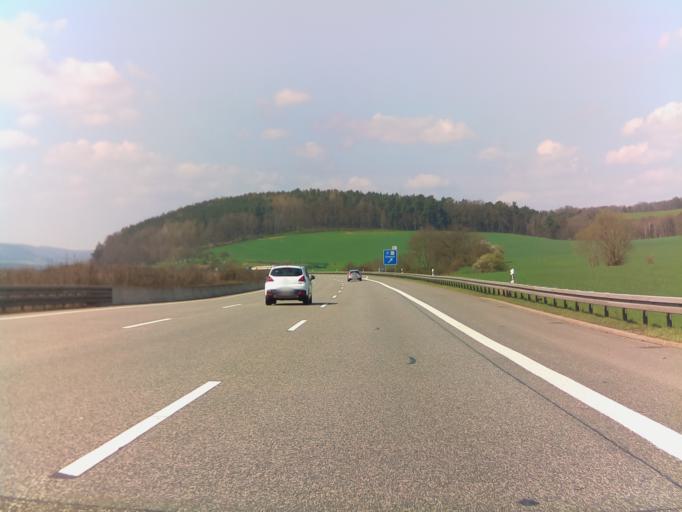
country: DE
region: Thuringia
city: Rausdorf
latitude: 50.8779
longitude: 11.6763
